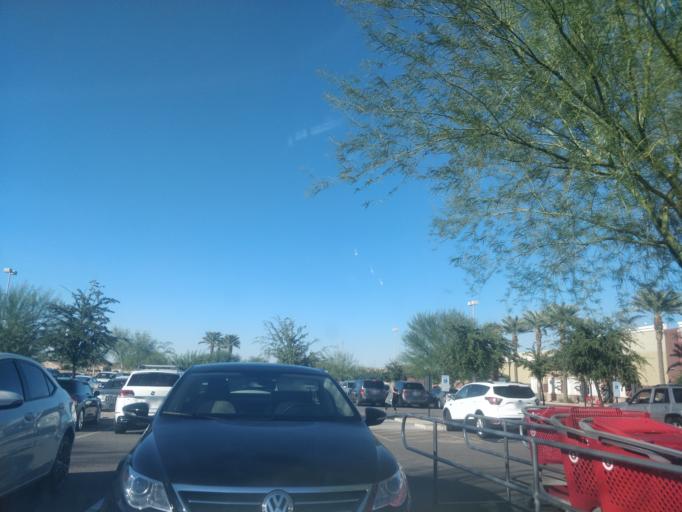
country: US
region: Arizona
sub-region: Maricopa County
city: Sun Lakes
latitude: 33.2499
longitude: -111.8387
